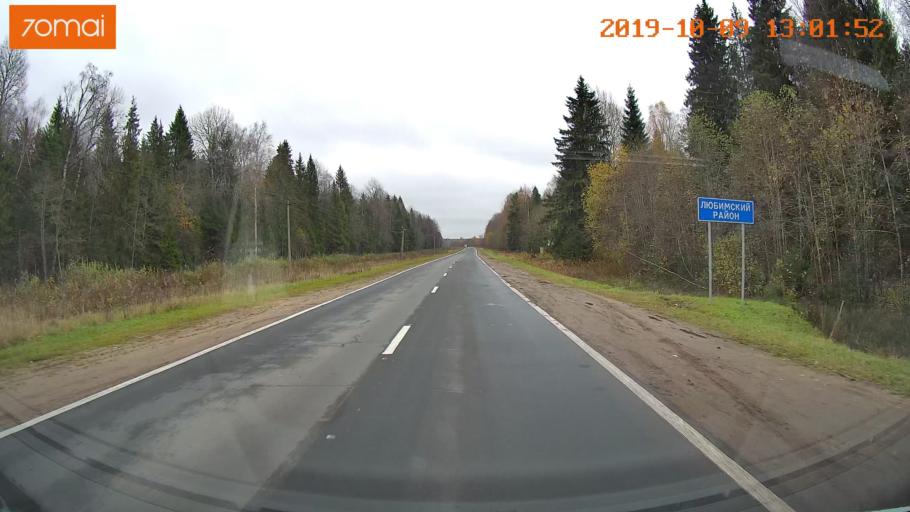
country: RU
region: Jaroslavl
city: Prechistoye
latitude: 58.3655
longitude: 40.4912
